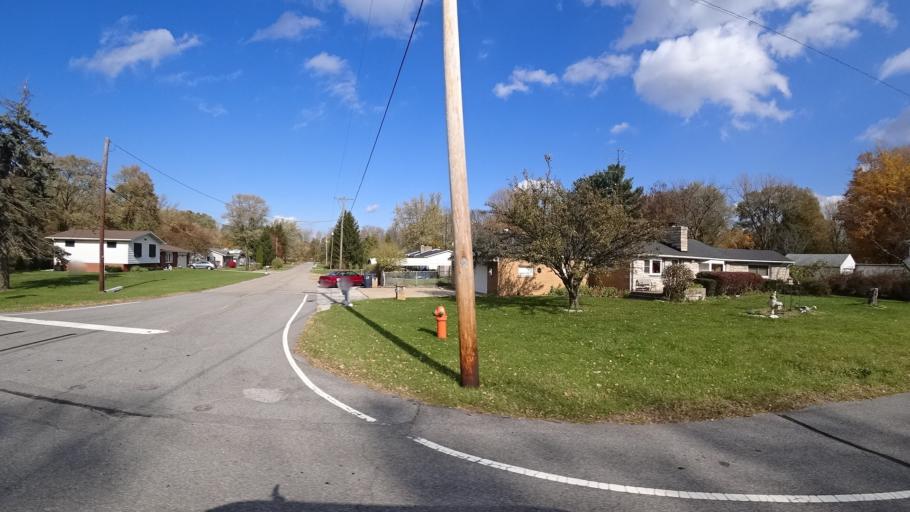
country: US
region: Indiana
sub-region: LaPorte County
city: Trail Creek
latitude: 41.7015
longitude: -86.8402
